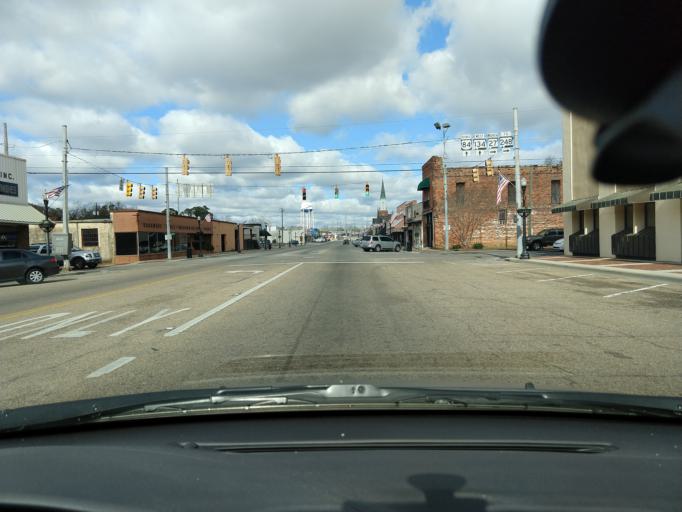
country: US
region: Alabama
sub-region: Coffee County
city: Enterprise
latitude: 31.3151
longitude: -85.8546
